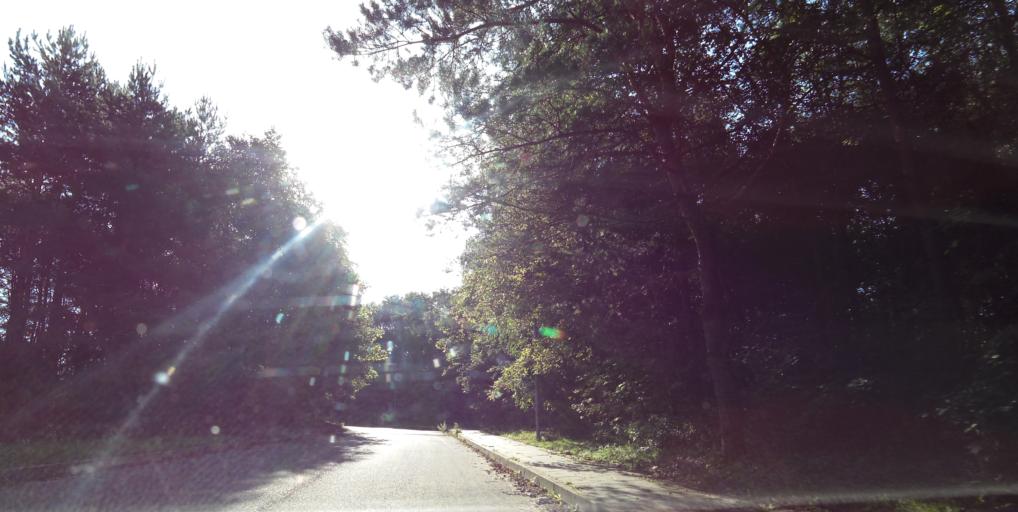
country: LT
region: Vilnius County
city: Seskine
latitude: 54.7038
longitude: 25.2388
